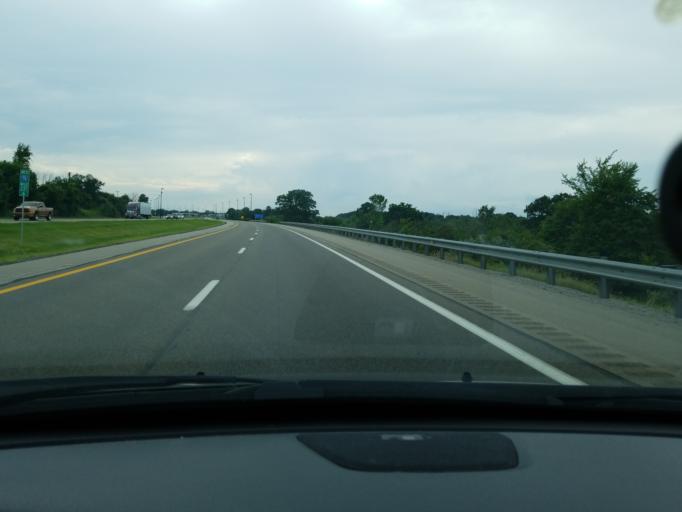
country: US
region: Ohio
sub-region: Mahoning County
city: New Middletown
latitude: 40.9370
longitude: -80.5781
